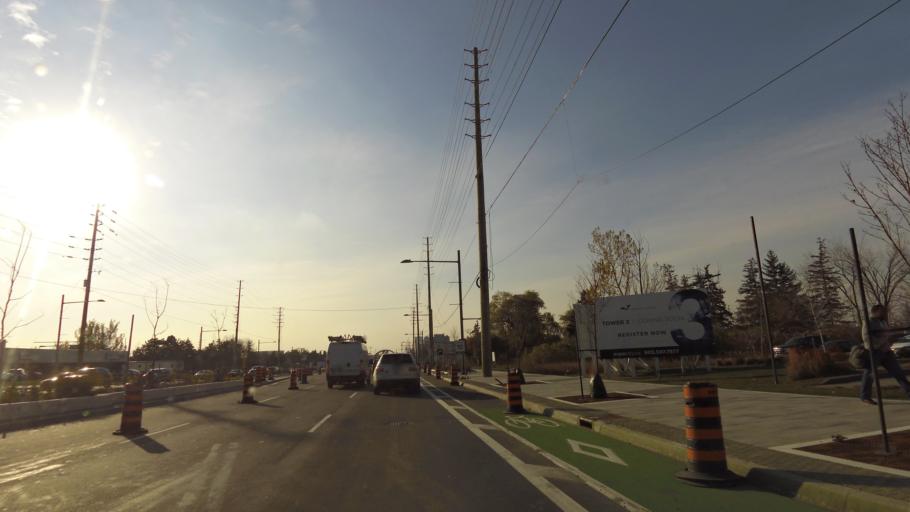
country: CA
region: Ontario
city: Concord
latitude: 43.7950
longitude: -79.5216
